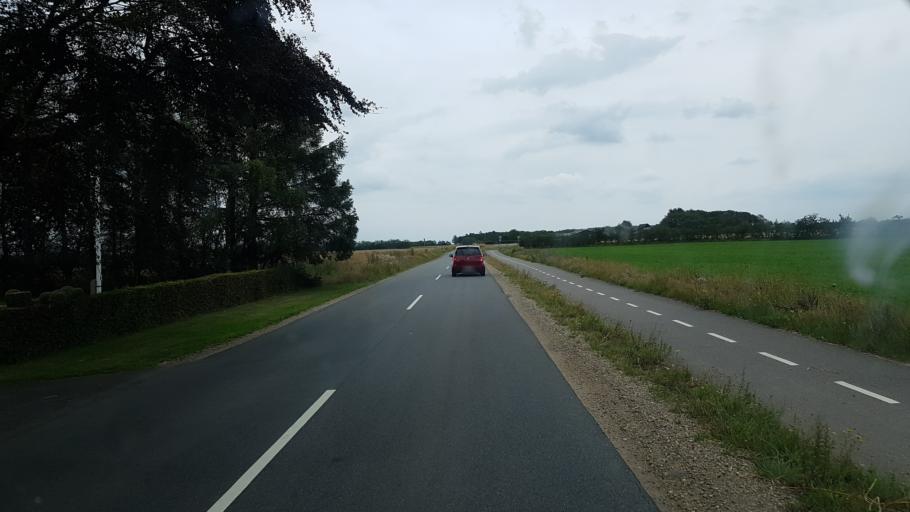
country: DK
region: South Denmark
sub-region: Varde Kommune
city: Olgod
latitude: 55.7166
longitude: 8.6170
